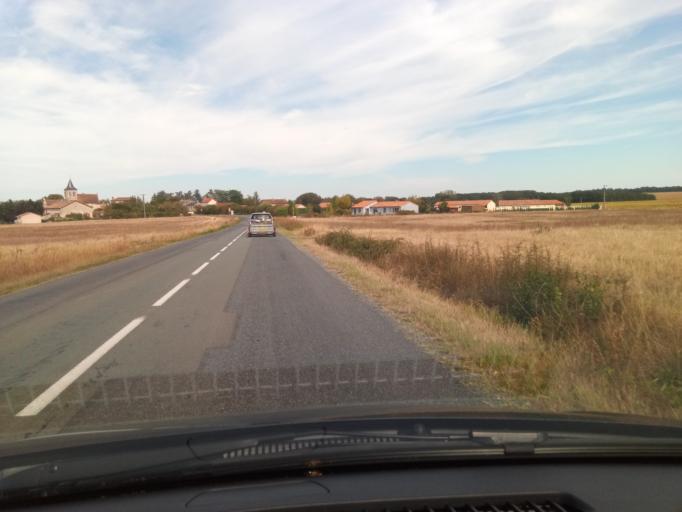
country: FR
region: Poitou-Charentes
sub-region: Departement de la Vienne
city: Terce
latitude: 46.5338
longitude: 0.5751
